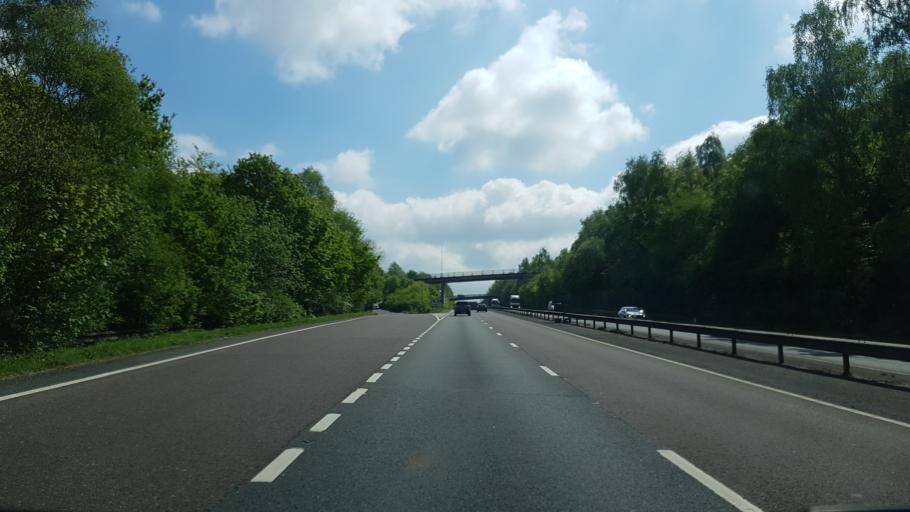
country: GB
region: England
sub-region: Kent
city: Tonbridge
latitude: 51.1830
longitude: 0.2589
